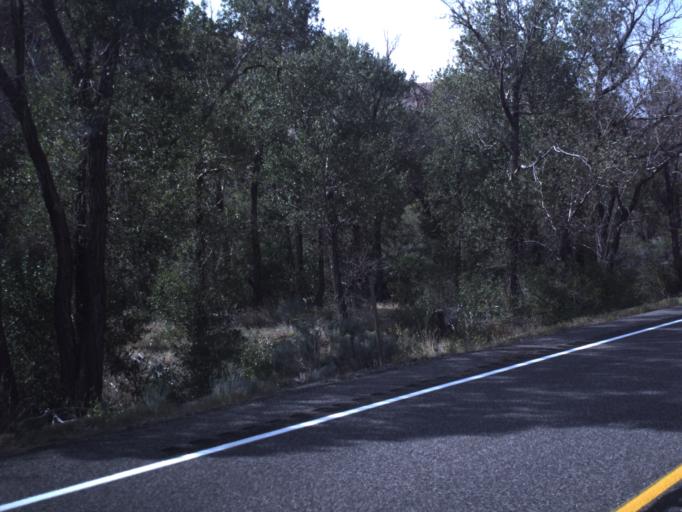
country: US
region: Utah
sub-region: Sevier County
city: Monroe
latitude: 38.5736
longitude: -112.2586
